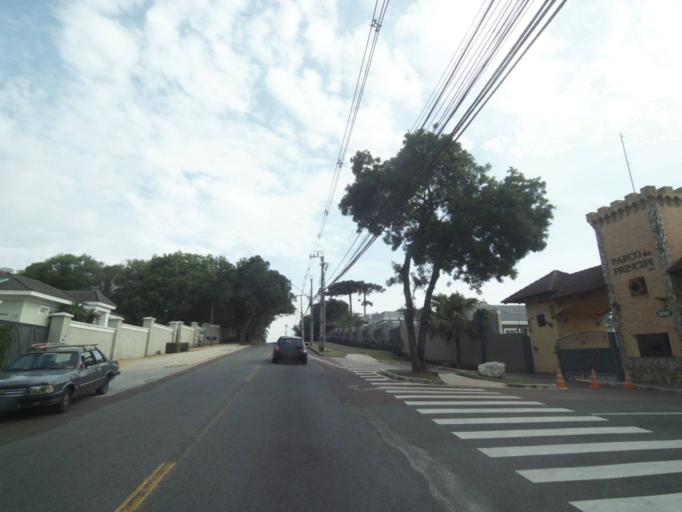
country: BR
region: Parana
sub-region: Curitiba
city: Curitiba
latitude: -25.4196
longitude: -49.3199
